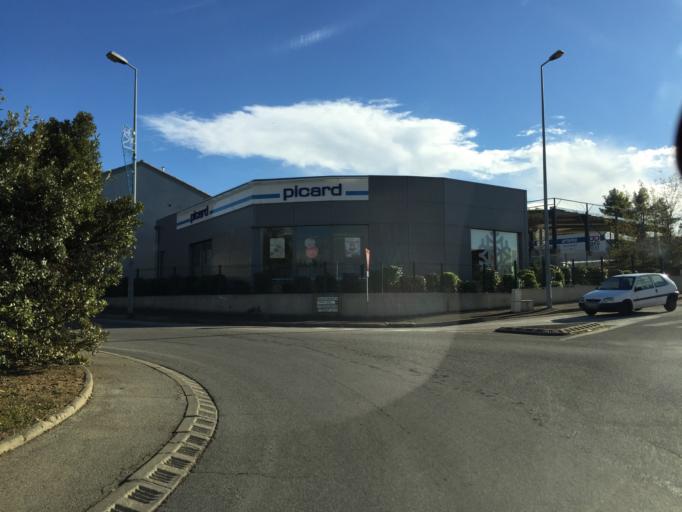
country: FR
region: Provence-Alpes-Cote d'Azur
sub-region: Departement du Vaucluse
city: Apt
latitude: 43.8828
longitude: 5.3814
